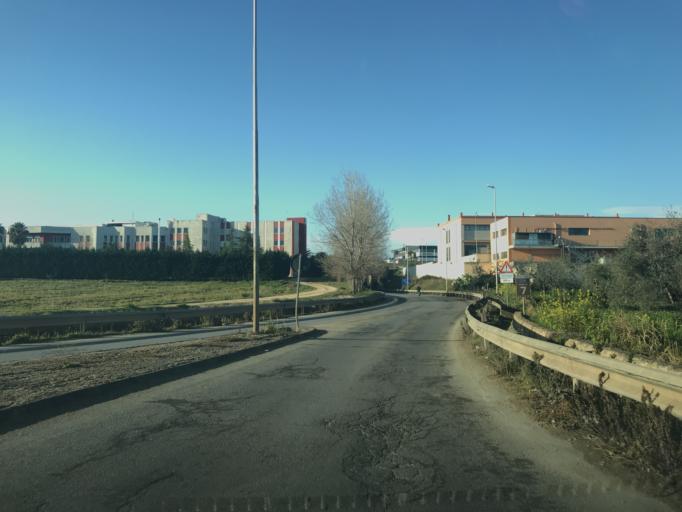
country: IT
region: Apulia
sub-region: Provincia di Bari
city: Corato
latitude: 41.1374
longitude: 16.4168
